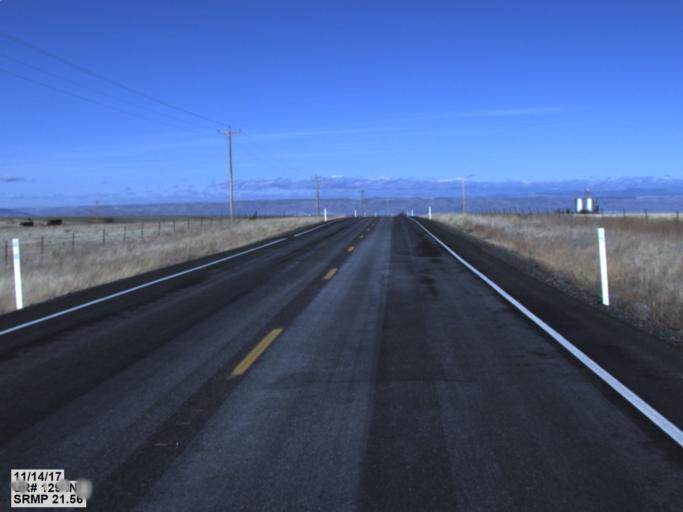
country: US
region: Washington
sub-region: Asotin County
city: Asotin
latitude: 46.1793
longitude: -117.0811
